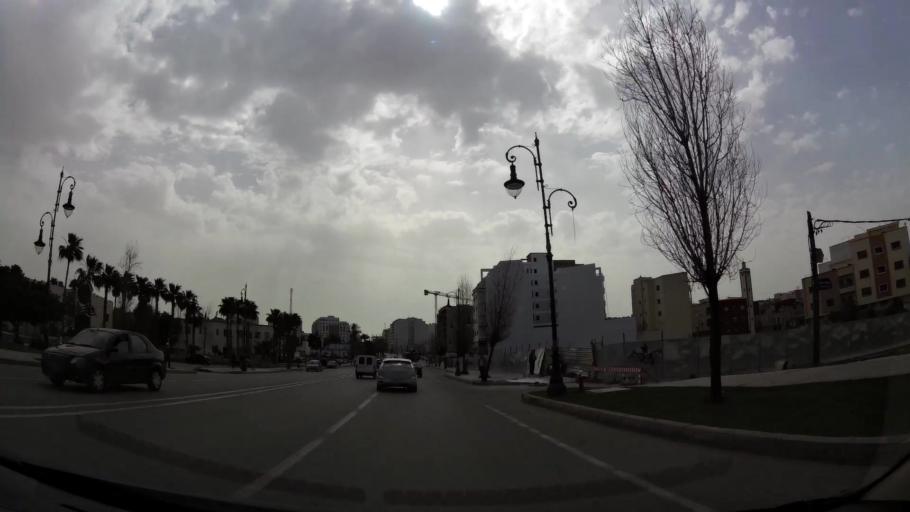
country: MA
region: Tanger-Tetouan
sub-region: Tanger-Assilah
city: Tangier
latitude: 35.7579
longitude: -5.8457
